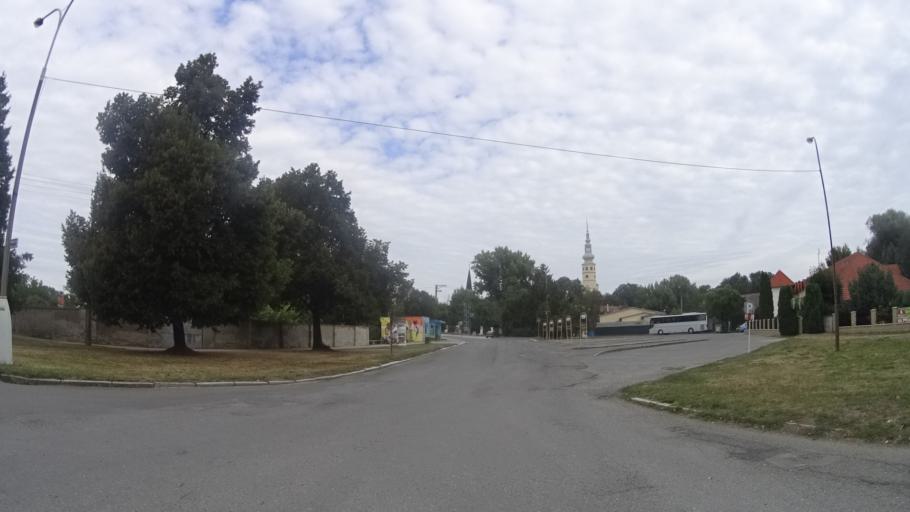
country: CZ
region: Olomoucky
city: Tovacov
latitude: 49.4263
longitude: 17.2913
